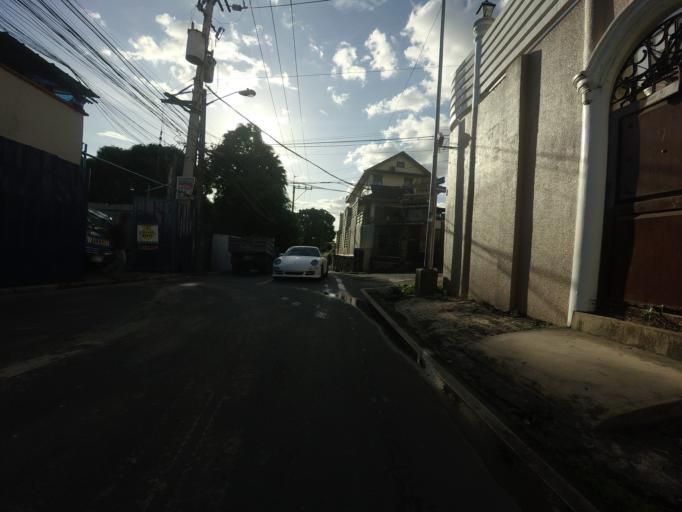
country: PH
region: Metro Manila
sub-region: San Juan
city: San Juan
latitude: 14.5960
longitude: 121.0353
